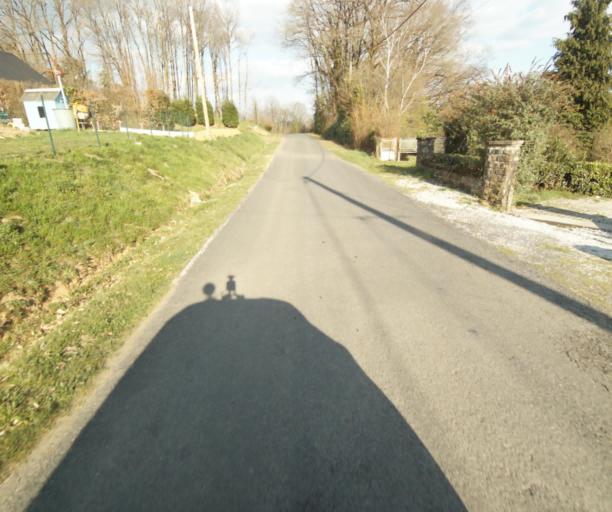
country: FR
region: Limousin
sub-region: Departement de la Correze
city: Saint-Clement
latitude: 45.3471
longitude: 1.6400
